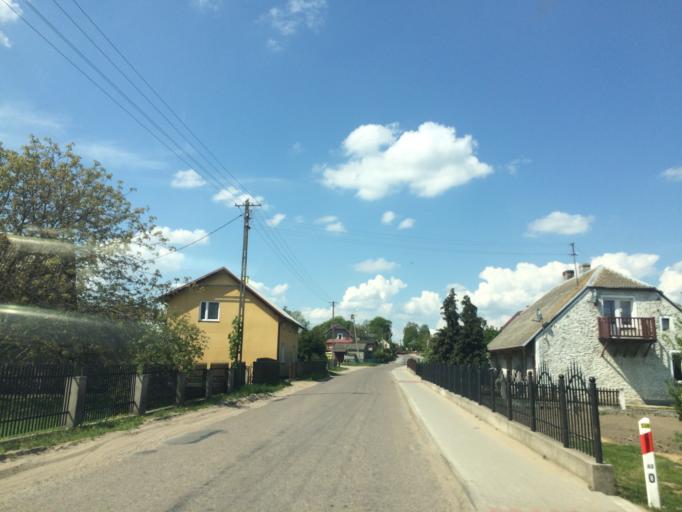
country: PL
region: Warmian-Masurian Voivodeship
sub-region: Powiat nowomiejski
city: Nowe Miasto Lubawskie
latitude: 53.4242
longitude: 19.6675
